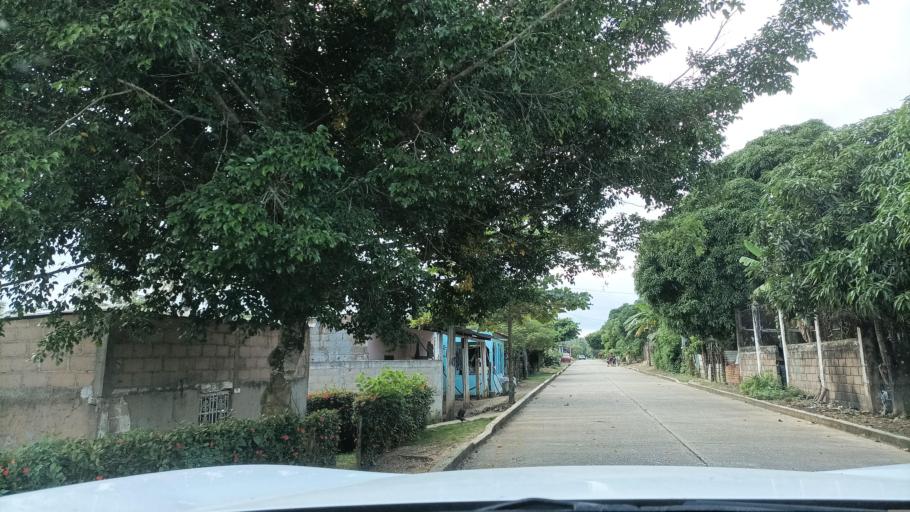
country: MX
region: Veracruz
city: Oluta
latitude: 17.8919
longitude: -94.8680
